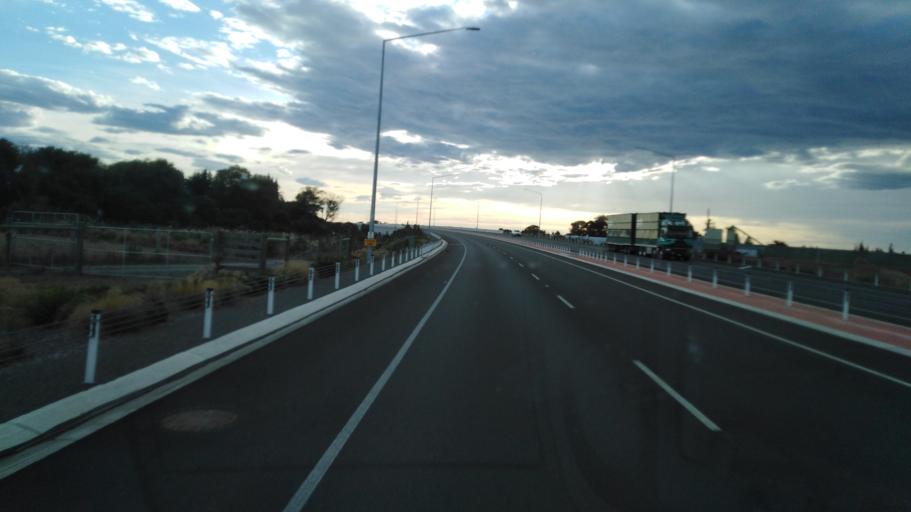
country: NZ
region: Canterbury
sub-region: Waimakariri District
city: Kaiapoi
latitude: -43.4373
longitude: 172.6306
